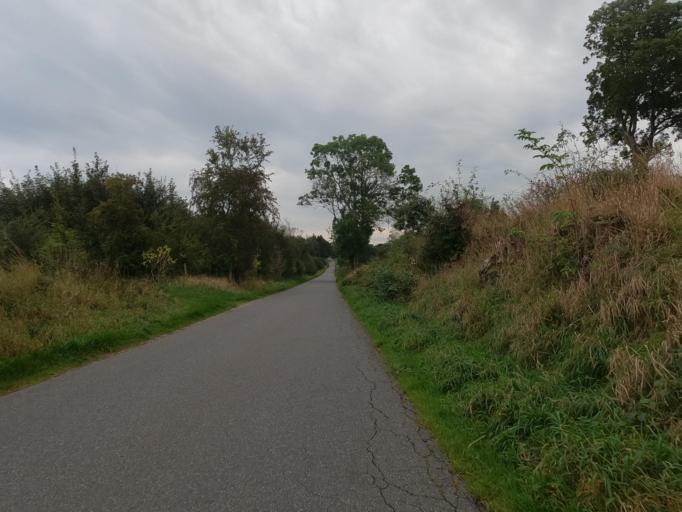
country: DE
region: Schleswig-Holstein
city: Neukirchen
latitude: 54.3042
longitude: 11.0460
